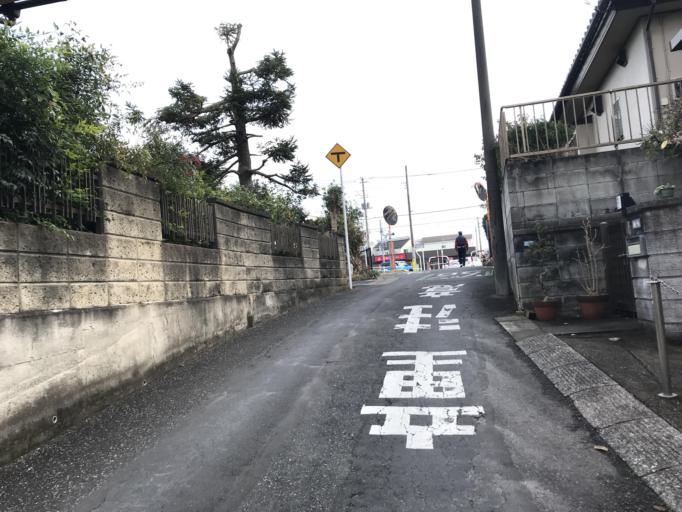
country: JP
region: Chiba
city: Shiroi
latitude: 35.7685
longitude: 140.0082
